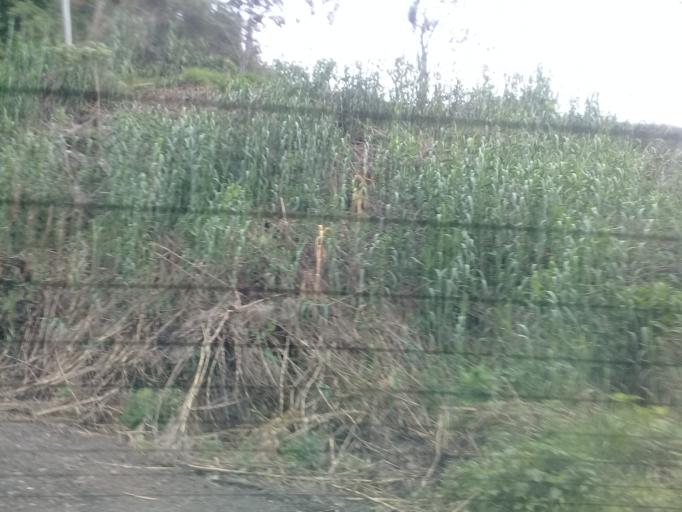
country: CO
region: Cundinamarca
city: Viani
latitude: 4.8451
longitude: -74.5499
